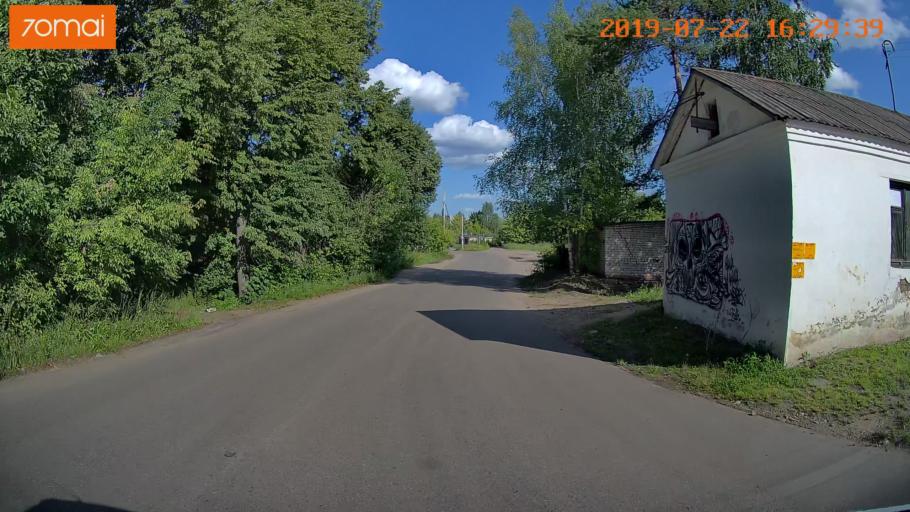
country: RU
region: Ivanovo
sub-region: Gorod Ivanovo
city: Ivanovo
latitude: 57.0308
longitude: 40.9481
